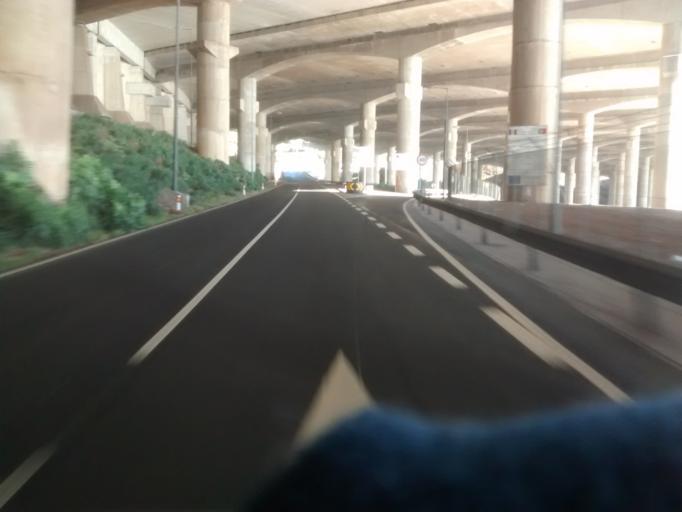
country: PT
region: Madeira
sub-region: Machico
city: Machico
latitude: 32.6997
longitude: -16.7708
